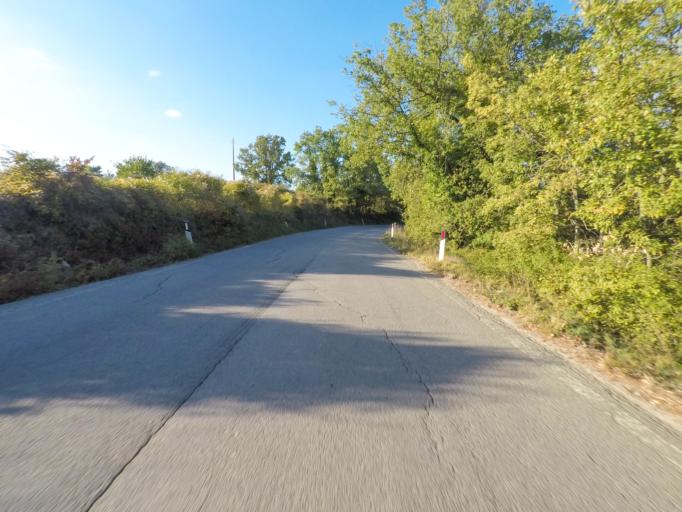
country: IT
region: Tuscany
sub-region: Provincia di Siena
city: Radda in Chianti
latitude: 43.4435
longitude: 11.3939
